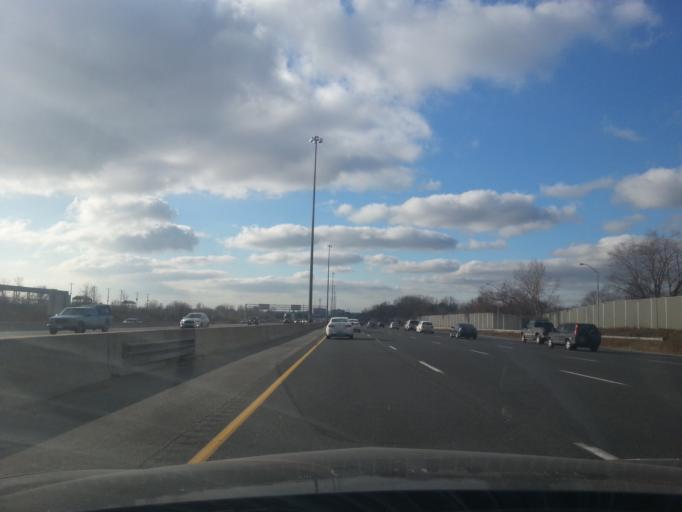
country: CA
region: Ontario
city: Ajax
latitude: 43.8489
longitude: -79.0420
